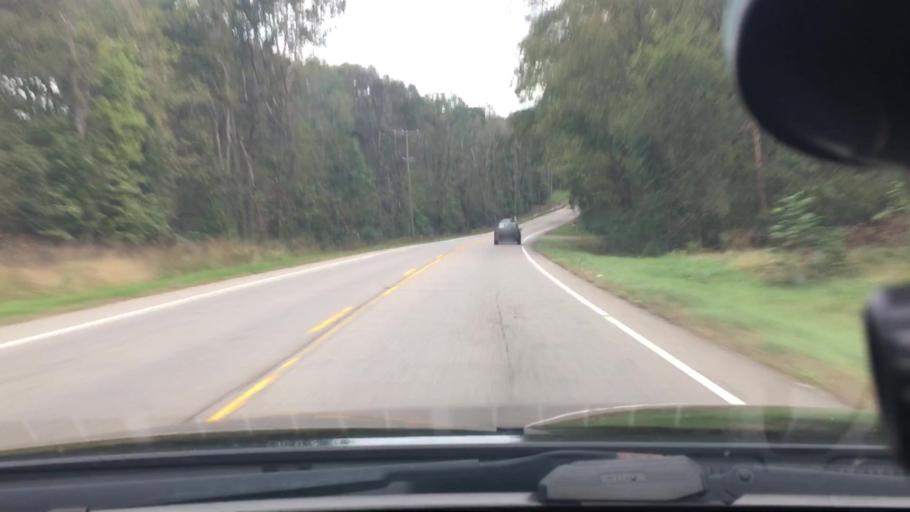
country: US
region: North Carolina
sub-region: Moore County
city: Robbins
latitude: 35.4043
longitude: -79.5693
